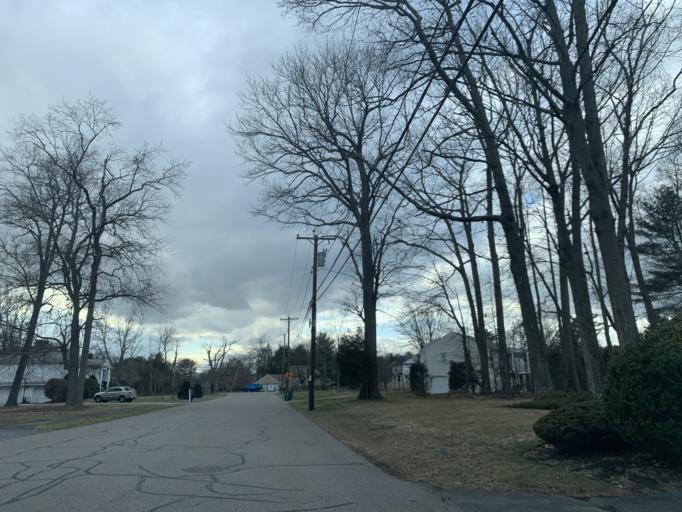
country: US
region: Massachusetts
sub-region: Norfolk County
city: Dedham
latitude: 42.2128
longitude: -71.1647
